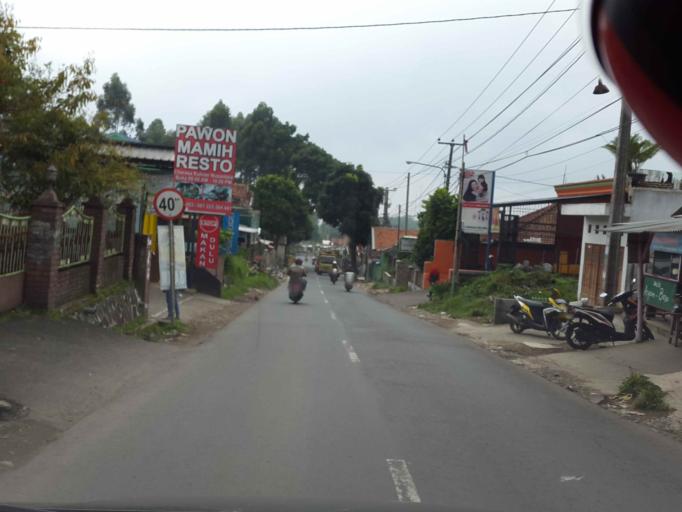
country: ID
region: West Java
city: Lembang
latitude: -6.7974
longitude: 107.5733
